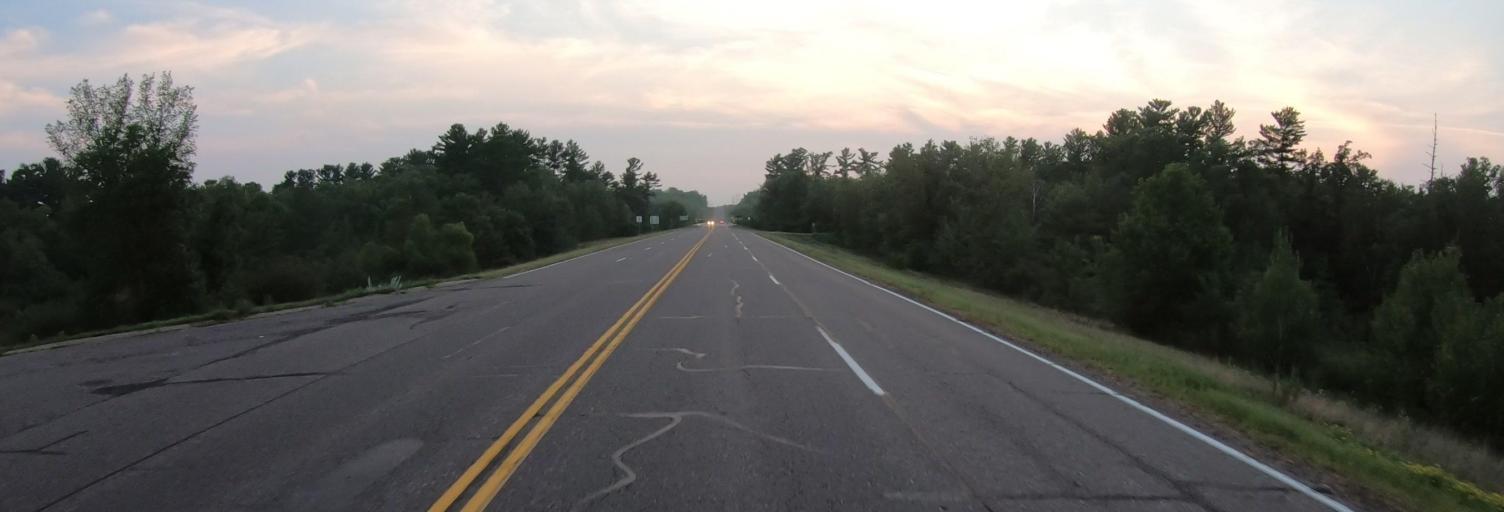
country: US
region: Wisconsin
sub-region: Burnett County
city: Grantsburg
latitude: 45.7733
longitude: -92.7761
